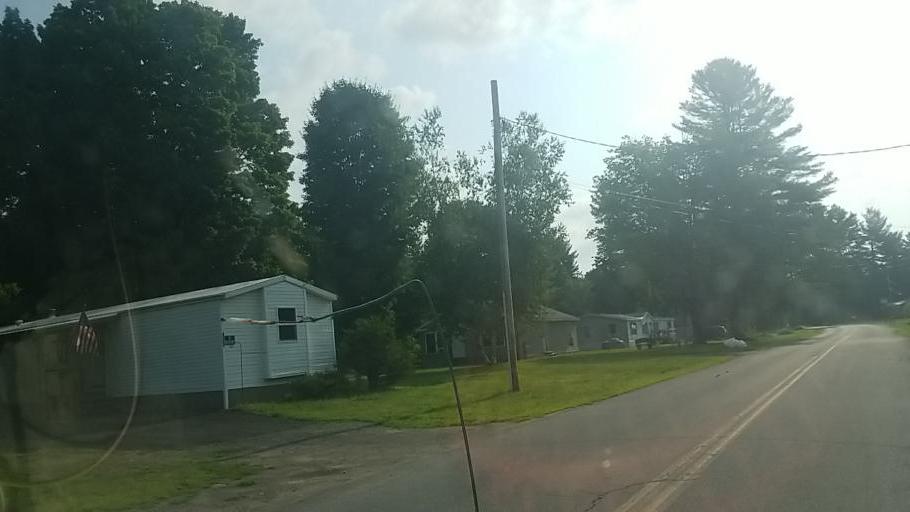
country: US
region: New York
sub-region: Fulton County
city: Broadalbin
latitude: 43.0702
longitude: -74.2503
